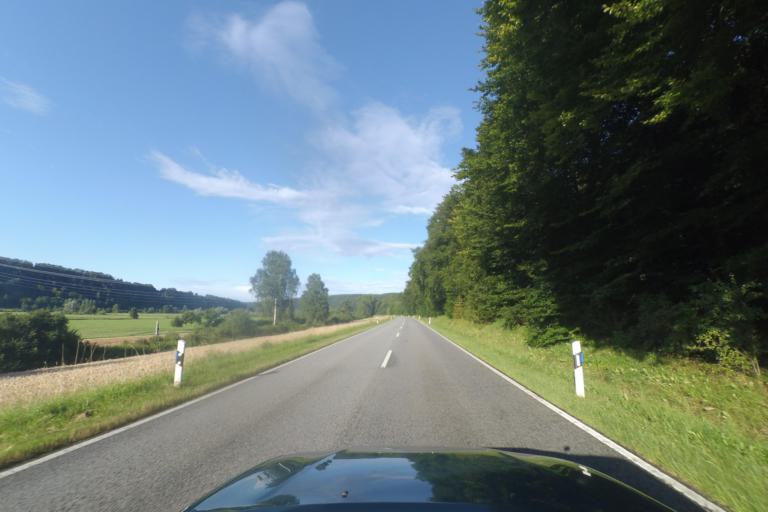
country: DE
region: Bavaria
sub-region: Upper Bavaria
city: Walting
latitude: 48.8954
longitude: 11.2788
